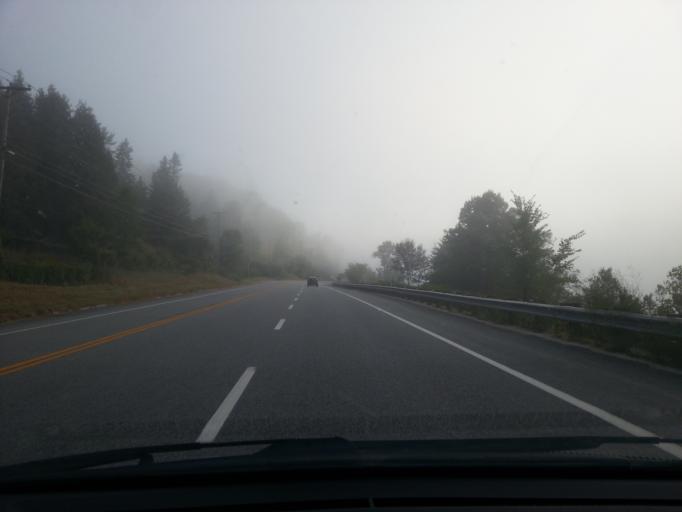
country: CA
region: Quebec
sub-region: Outaouais
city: Wakefield
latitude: 45.6983
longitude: -75.9314
